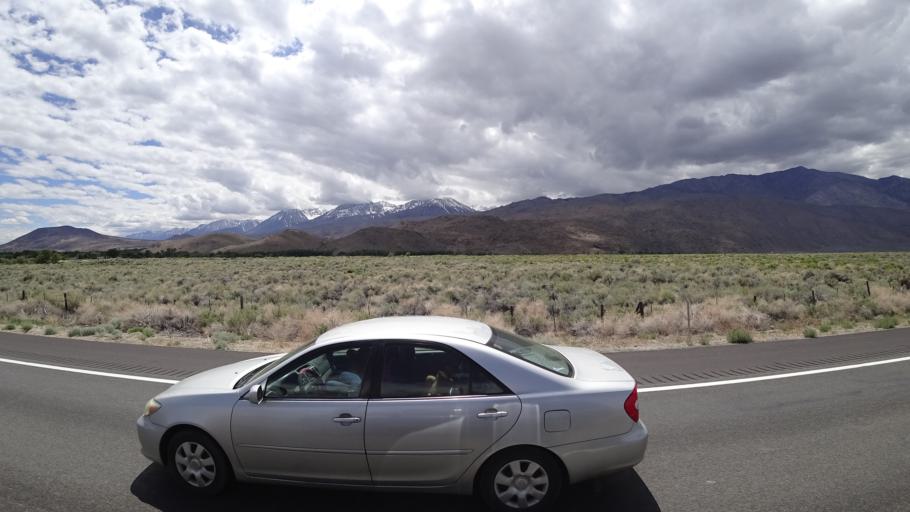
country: US
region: California
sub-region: Inyo County
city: Big Pine
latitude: 37.1907
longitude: -118.3072
